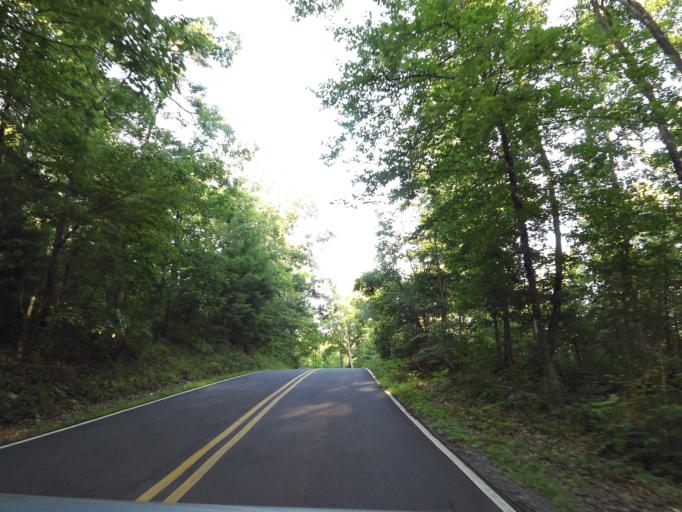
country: US
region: Tennessee
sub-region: Blount County
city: Maryville
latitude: 35.6423
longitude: -83.9155
